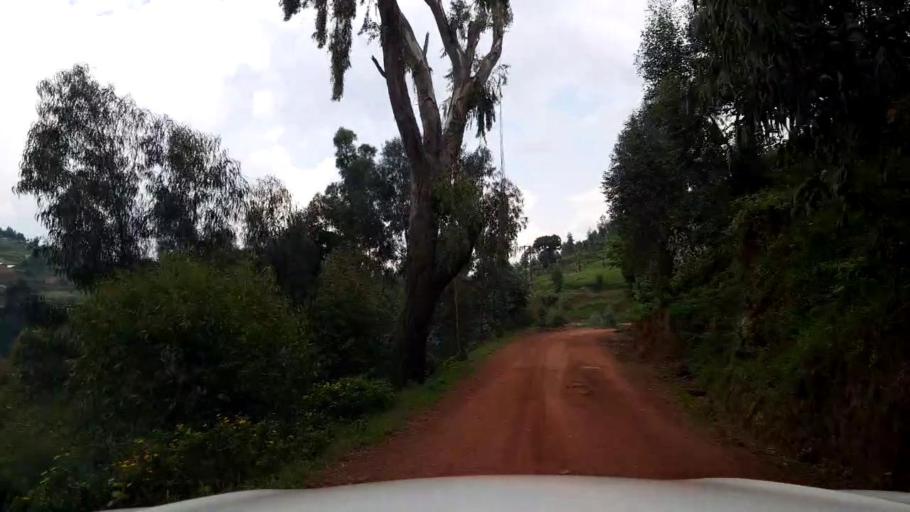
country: RW
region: Northern Province
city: Byumba
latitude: -1.5248
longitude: 29.9533
